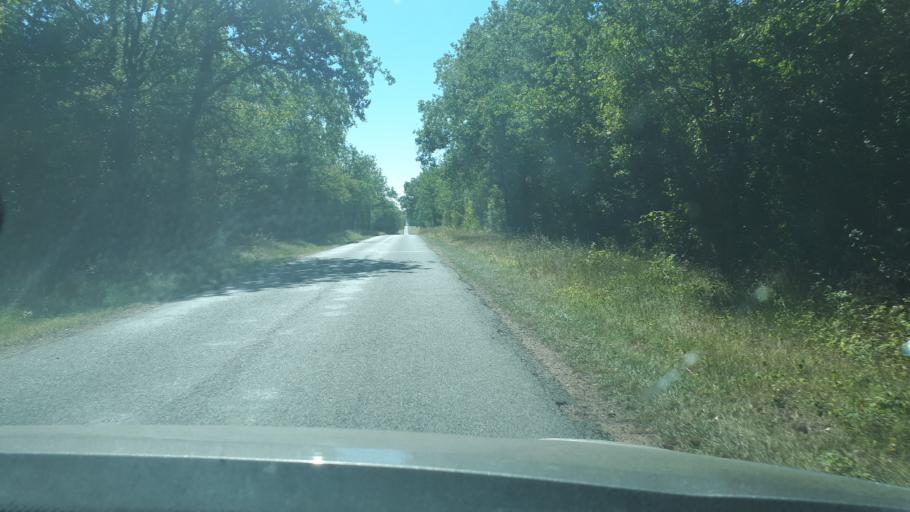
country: FR
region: Centre
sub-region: Departement du Cher
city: Sancerre
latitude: 47.2374
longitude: 2.7566
